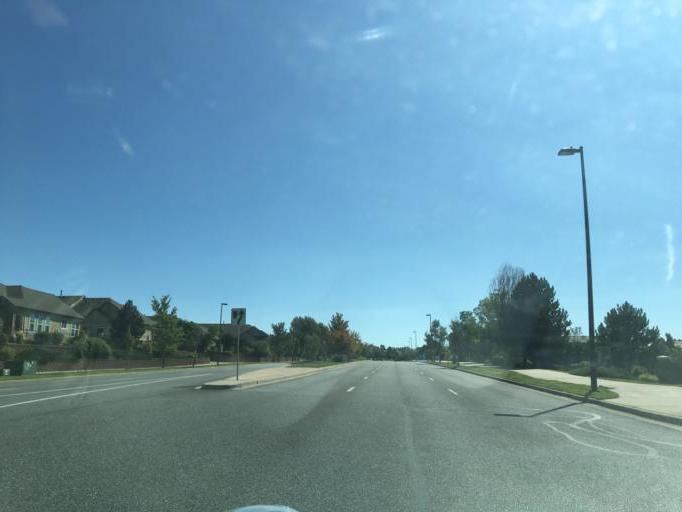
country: US
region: Colorado
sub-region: Douglas County
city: Parker
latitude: 39.5949
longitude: -104.7305
